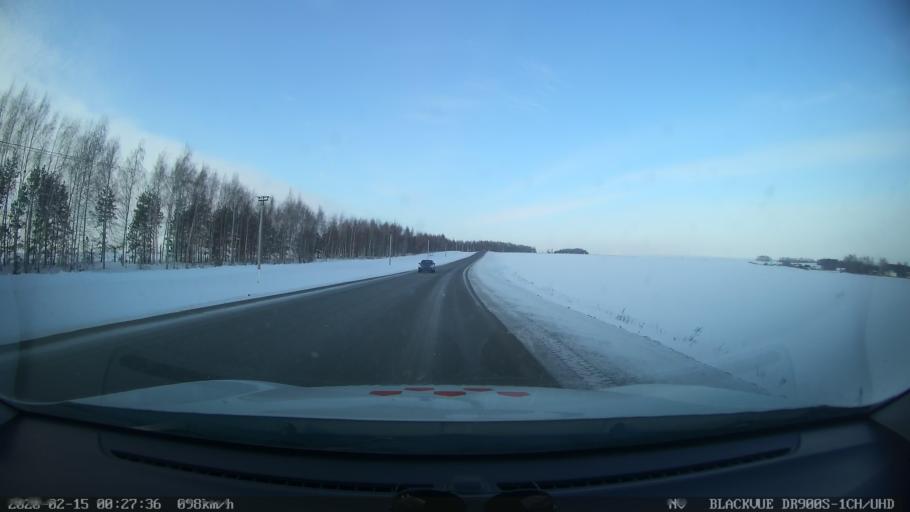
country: RU
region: Tatarstan
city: Verkhniy Uslon
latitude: 55.6304
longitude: 48.8730
